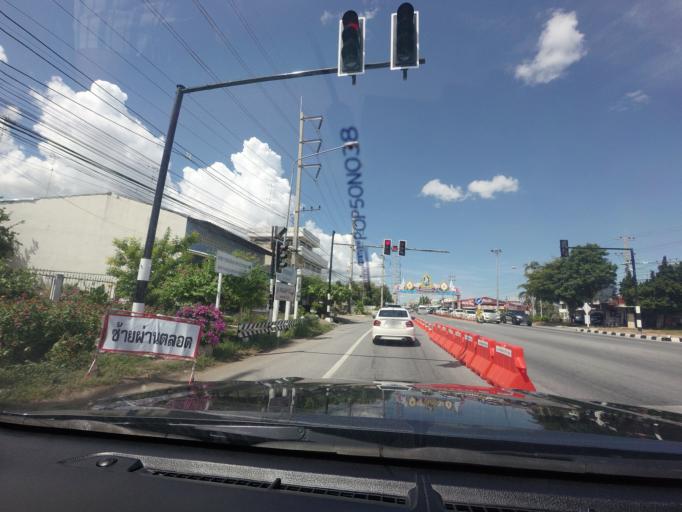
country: TH
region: Kanchanaburi
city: Tha Muang
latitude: 14.0505
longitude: 99.6266
